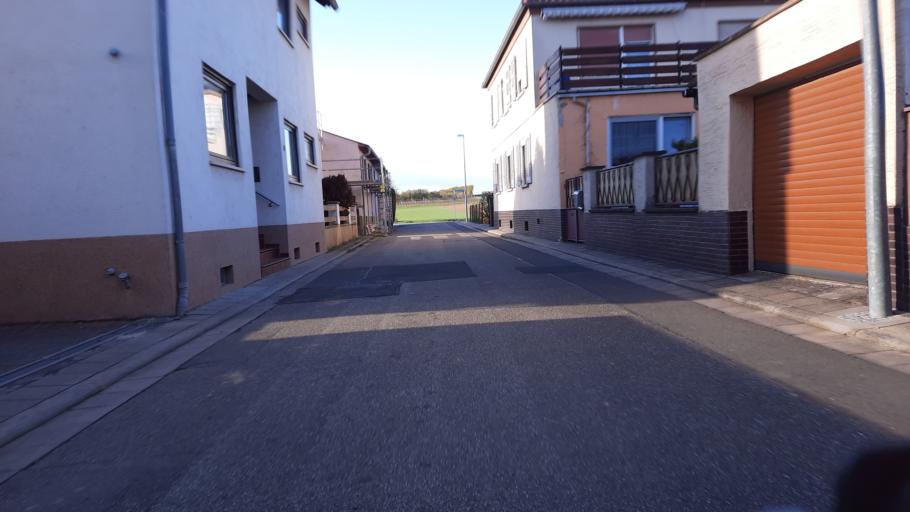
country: DE
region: Rheinland-Pfalz
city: Offstein
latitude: 49.6072
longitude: 8.2668
